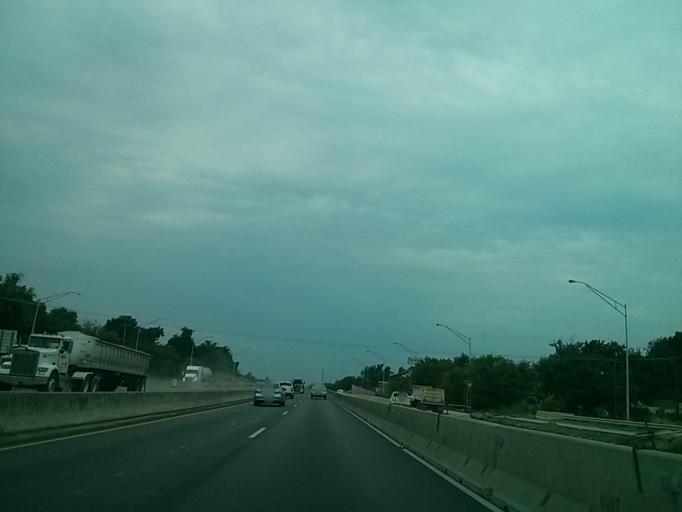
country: US
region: Oklahoma
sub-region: Tulsa County
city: Tulsa
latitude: 36.1594
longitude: -95.9246
